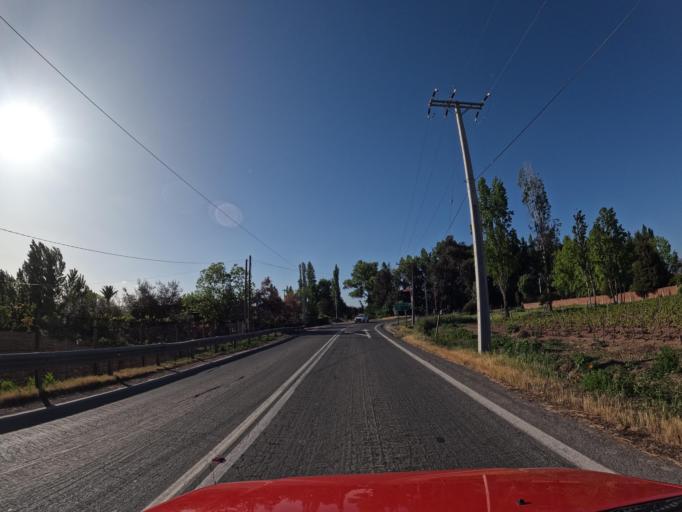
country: CL
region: Maule
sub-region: Provincia de Curico
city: Teno
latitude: -34.7563
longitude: -71.2399
